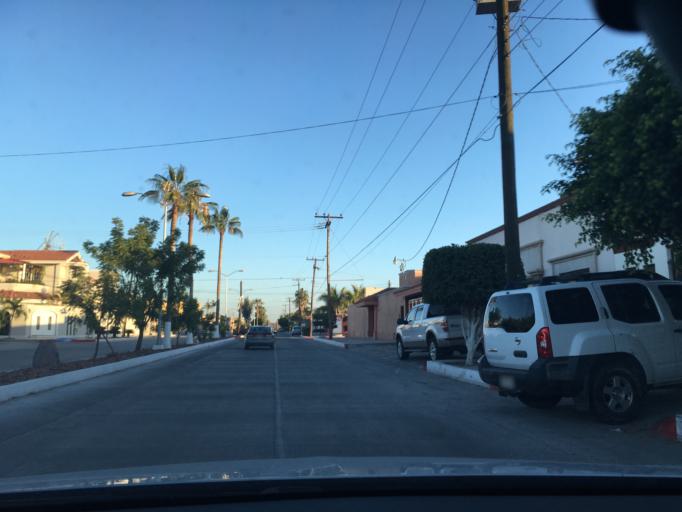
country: MX
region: Baja California Sur
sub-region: La Paz
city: La Paz
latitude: 24.1272
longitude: -110.3080
